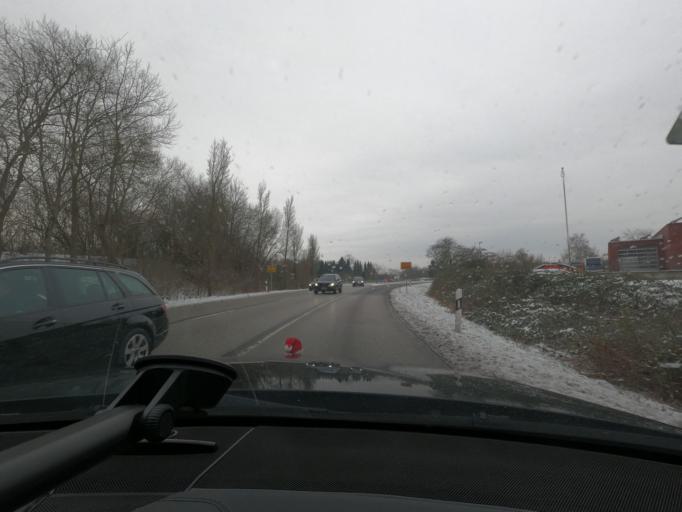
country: DE
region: Schleswig-Holstein
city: Flensburg
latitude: 54.7760
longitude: 9.4144
